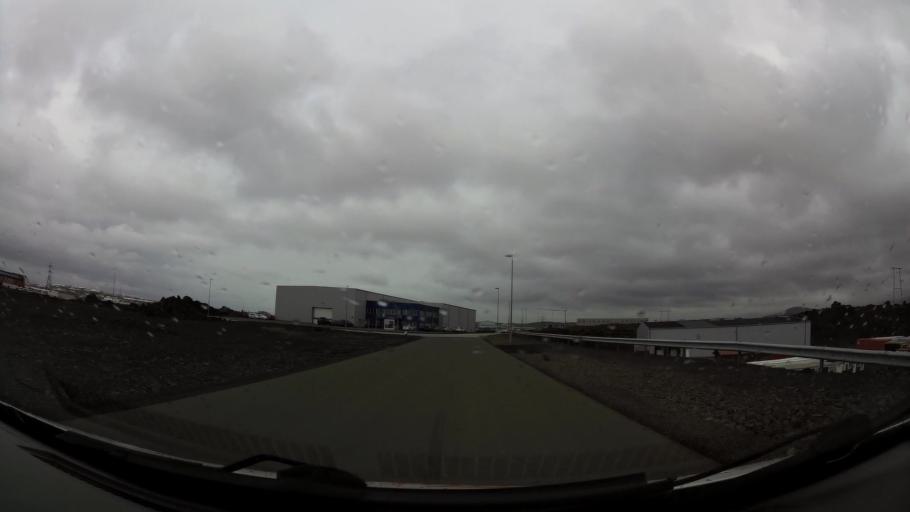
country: IS
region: Capital Region
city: Alftanes
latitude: 64.0374
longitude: -22.0010
